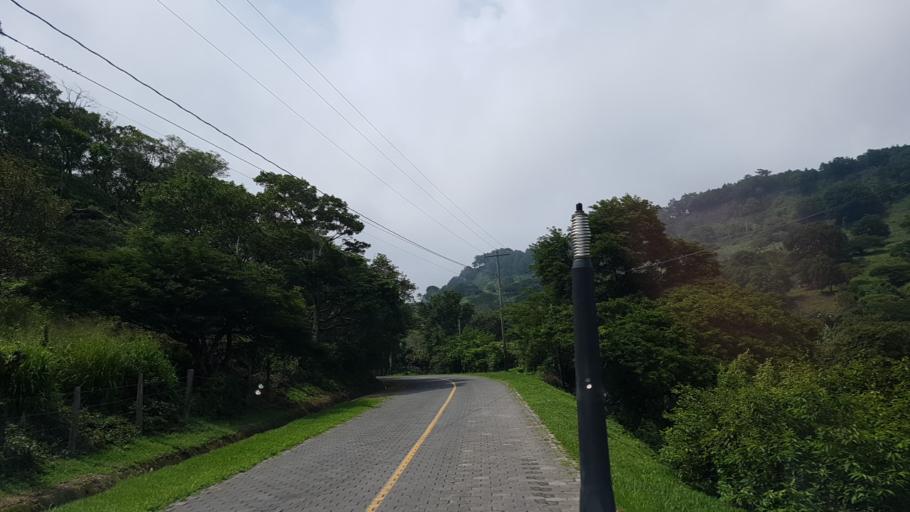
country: NI
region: Leon
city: Santa Rosa del Penon
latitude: 12.9398
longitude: -86.3404
